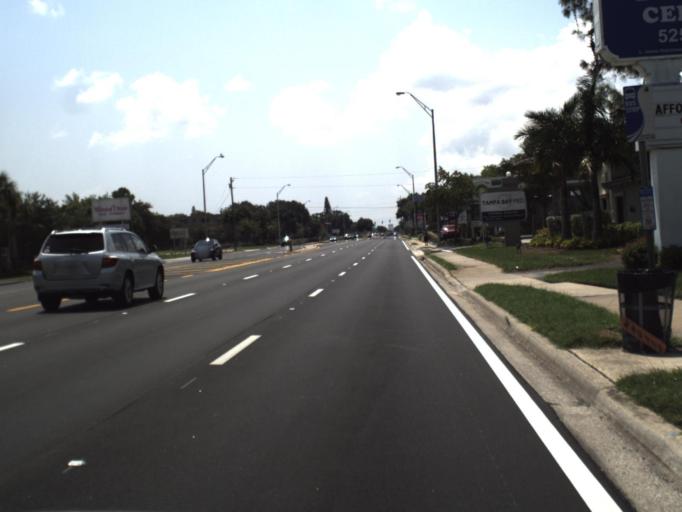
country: US
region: Florida
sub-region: Pinellas County
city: Gandy
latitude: 27.8415
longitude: -82.6388
